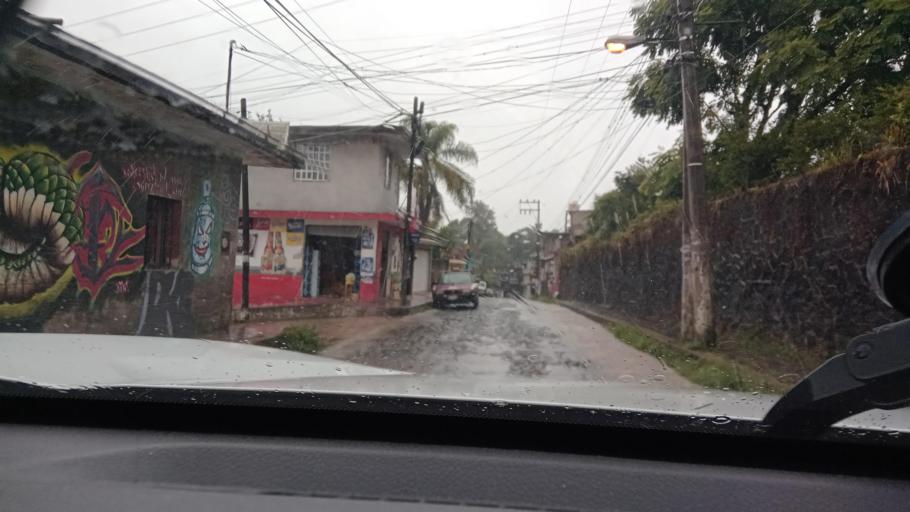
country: MX
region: Veracruz
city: Coatepec
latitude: 19.4585
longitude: -96.9717
